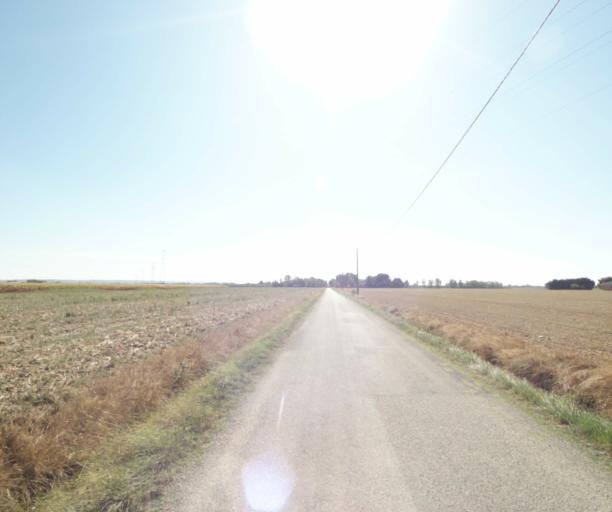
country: FR
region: Midi-Pyrenees
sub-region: Departement du Tarn-et-Garonne
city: Verdun-sur-Garonne
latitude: 43.8366
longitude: 1.2170
